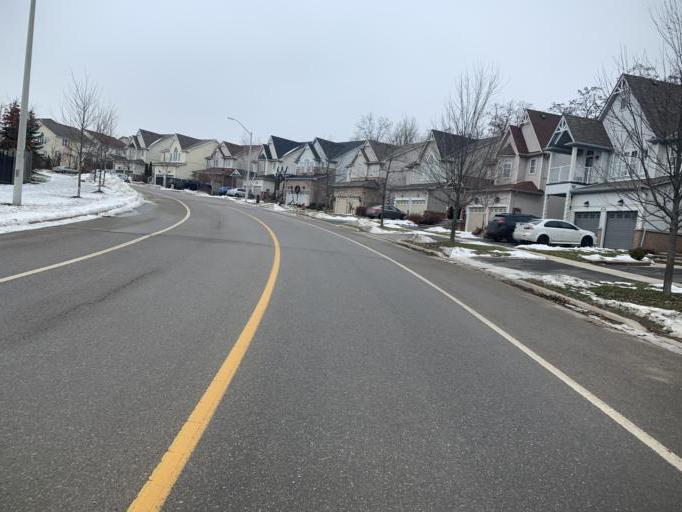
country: CA
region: Ontario
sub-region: Halton
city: Milton
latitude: 43.6609
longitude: -79.9222
